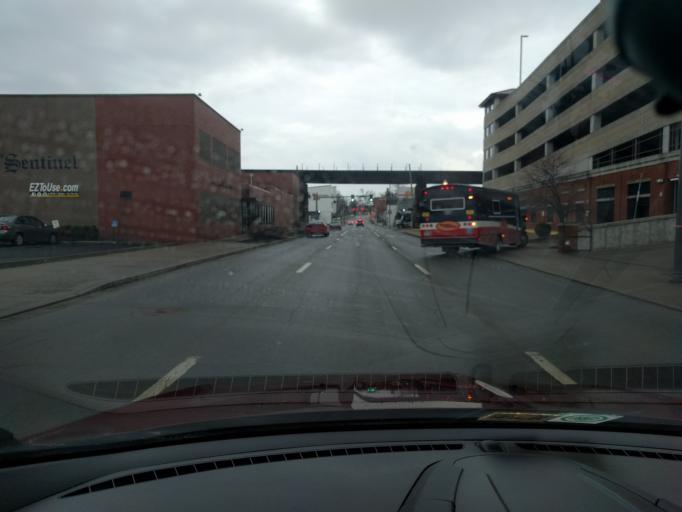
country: US
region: West Virginia
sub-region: Wood County
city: Parkersburg
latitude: 39.2669
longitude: -81.5609
